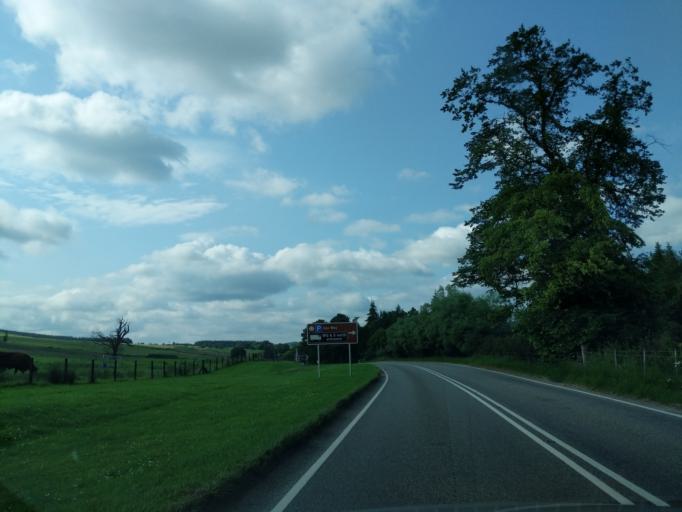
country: GB
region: Scotland
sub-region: Moray
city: Dufftown
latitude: 57.4585
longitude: -3.1319
